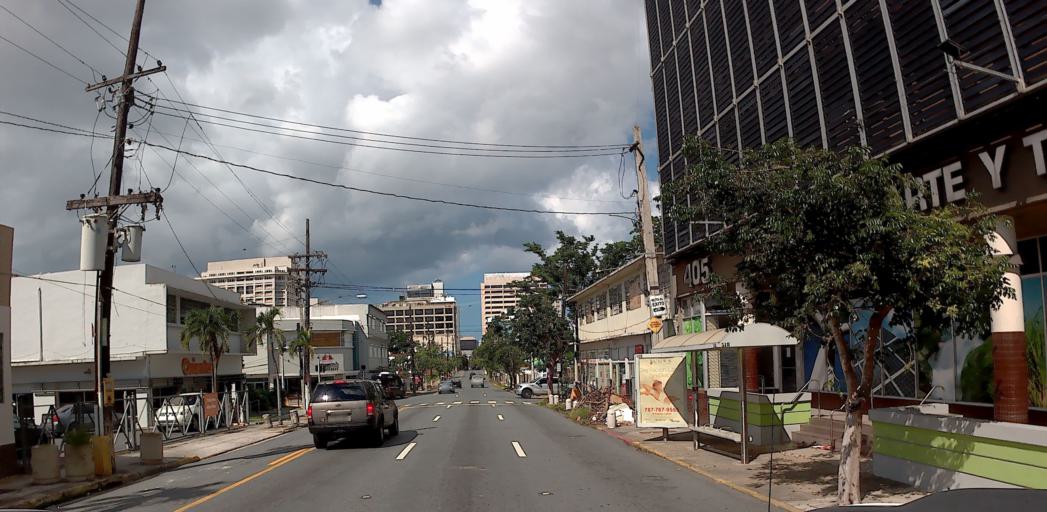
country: PR
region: Catano
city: Catano
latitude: 18.4208
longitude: -66.0566
